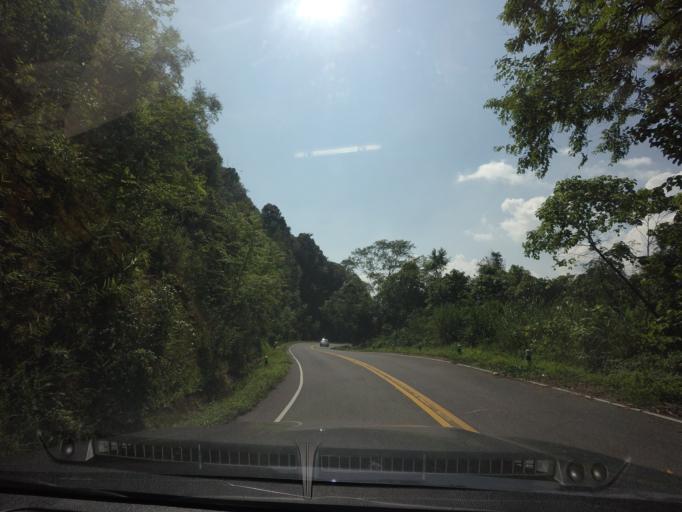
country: TH
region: Nan
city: Bo Kluea
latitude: 19.0397
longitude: 101.0873
